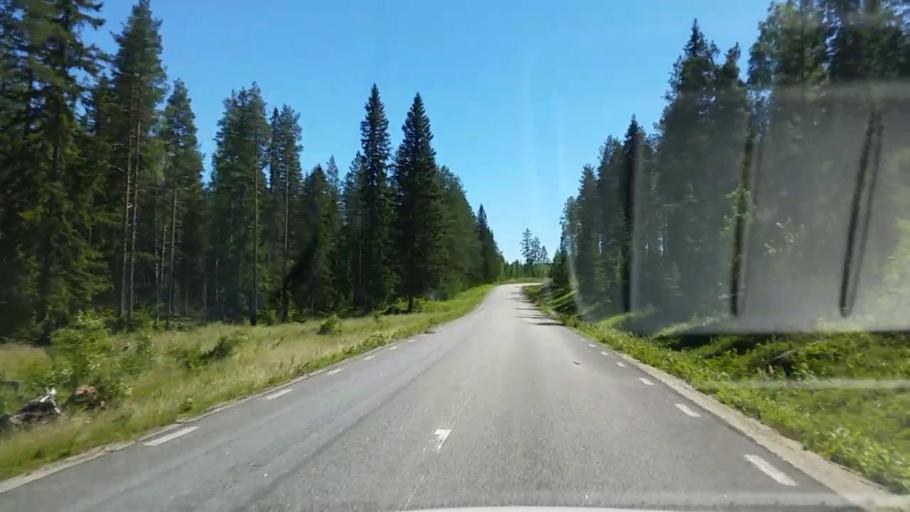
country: SE
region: Gaevleborg
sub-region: Ljusdals Kommun
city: Farila
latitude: 61.6481
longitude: 15.5904
